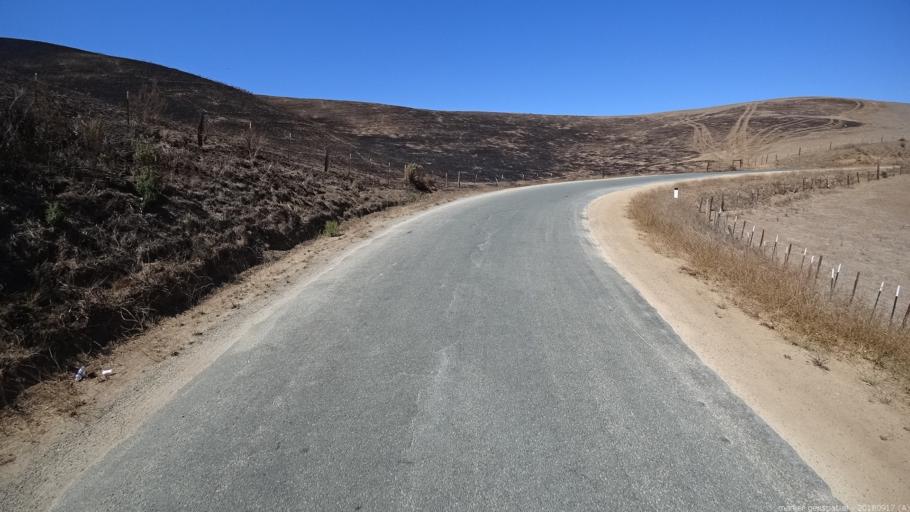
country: US
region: California
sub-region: San Benito County
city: San Juan Bautista
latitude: 36.8104
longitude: -121.5836
